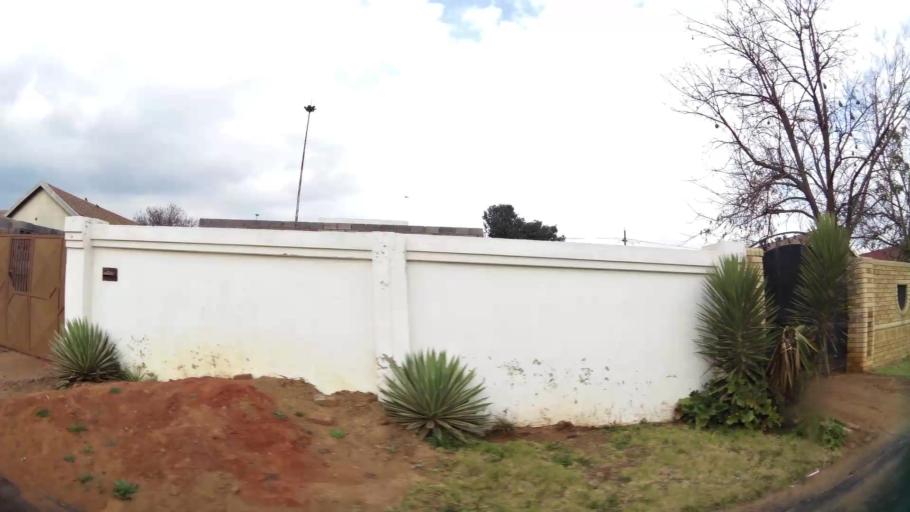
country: ZA
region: Gauteng
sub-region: City of Johannesburg Metropolitan Municipality
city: Soweto
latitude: -26.2426
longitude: 27.8114
